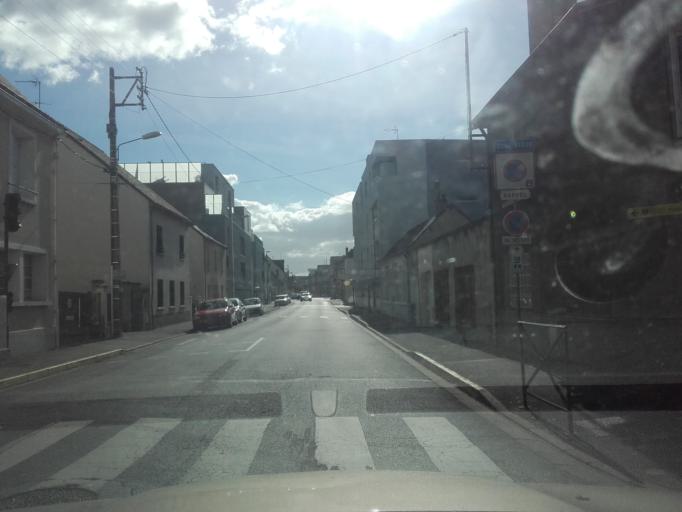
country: FR
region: Centre
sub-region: Departement d'Indre-et-Loire
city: Saint-Pierre-des-Corps
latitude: 47.3884
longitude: 0.7203
